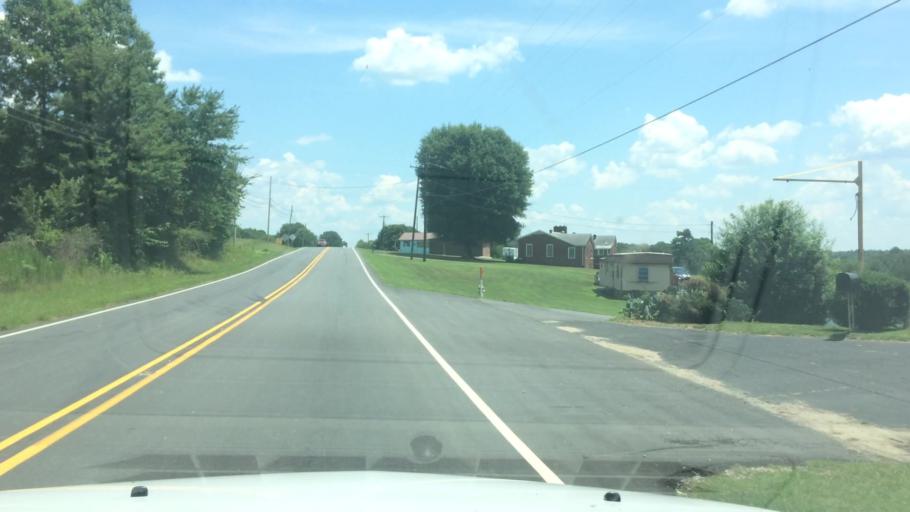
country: US
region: North Carolina
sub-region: Alexander County
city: Taylorsville
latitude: 35.9197
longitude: -81.2284
